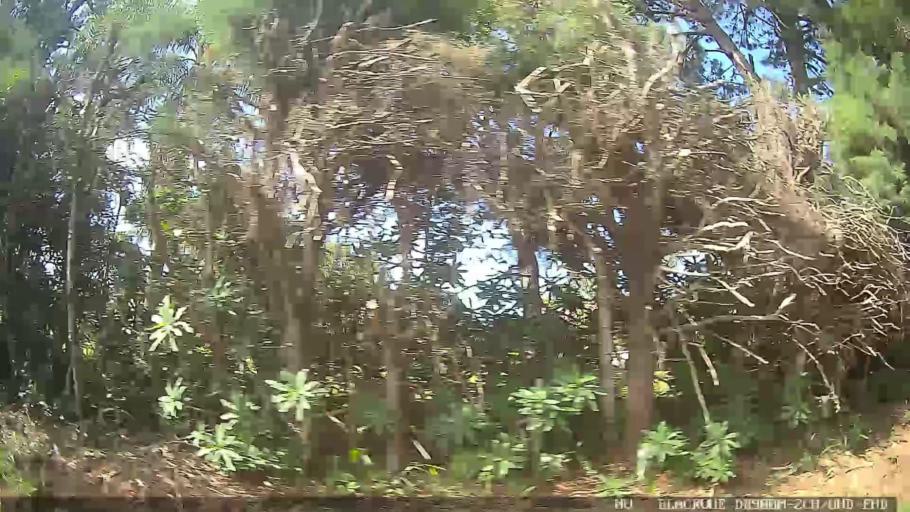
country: BR
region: Sao Paulo
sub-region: Jarinu
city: Jarinu
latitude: -23.0746
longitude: -46.6511
